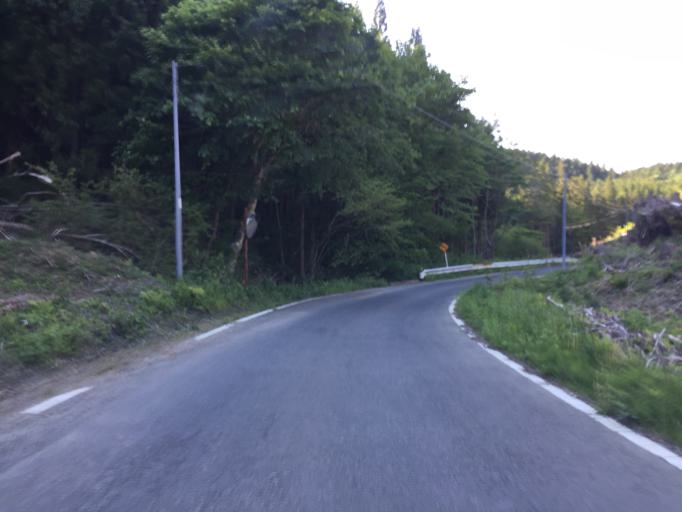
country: JP
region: Ibaraki
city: Kitaibaraki
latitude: 36.8991
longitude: 140.5946
